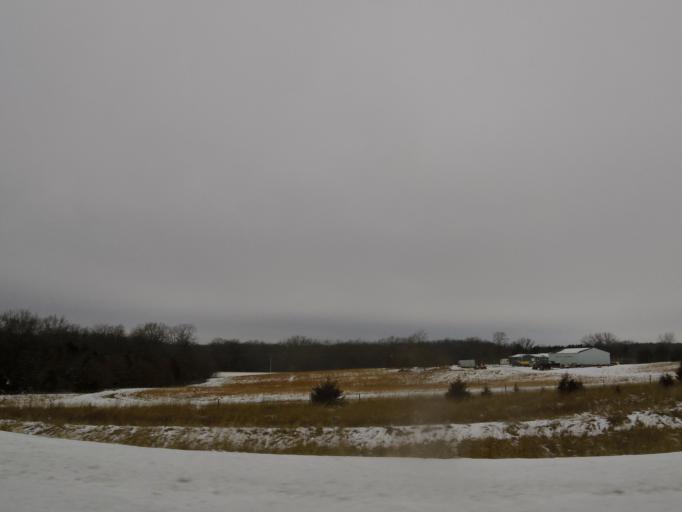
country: US
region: Illinois
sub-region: Hancock County
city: Nauvoo
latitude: 40.6033
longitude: -91.5617
